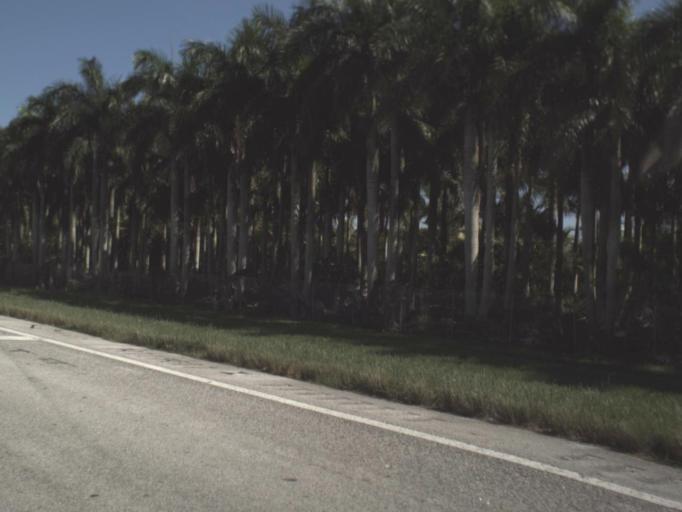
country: US
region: Florida
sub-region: Miami-Dade County
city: Goulds
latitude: 25.5409
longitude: -80.3636
